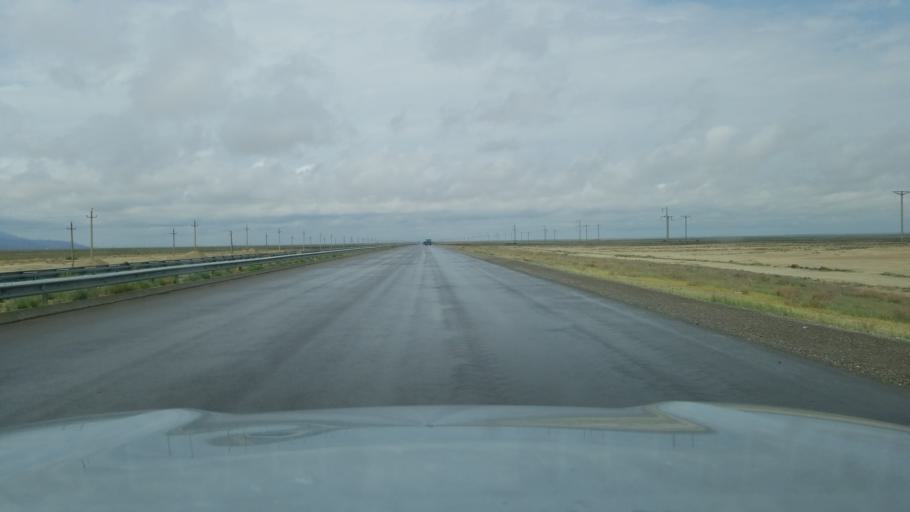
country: TM
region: Balkan
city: Gazanjyk
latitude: 39.1834
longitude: 55.7992
